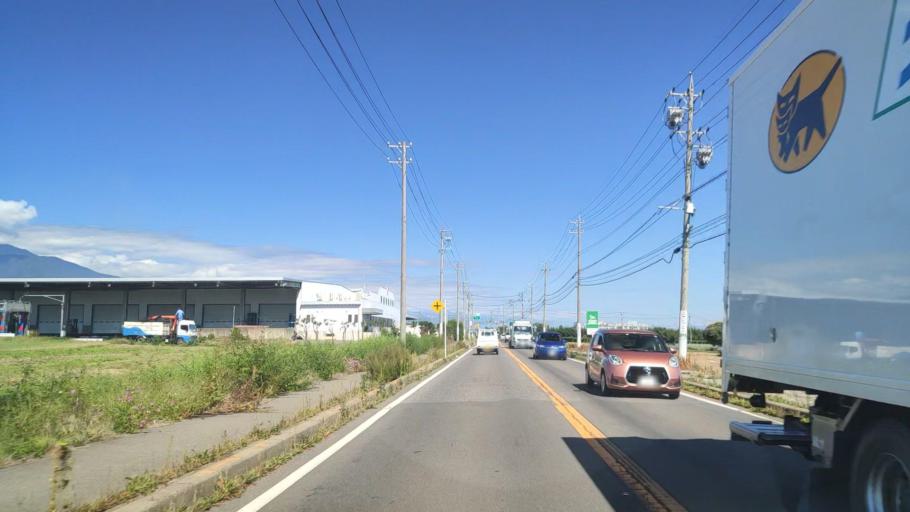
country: JP
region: Nagano
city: Matsumoto
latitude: 36.1981
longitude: 137.9029
